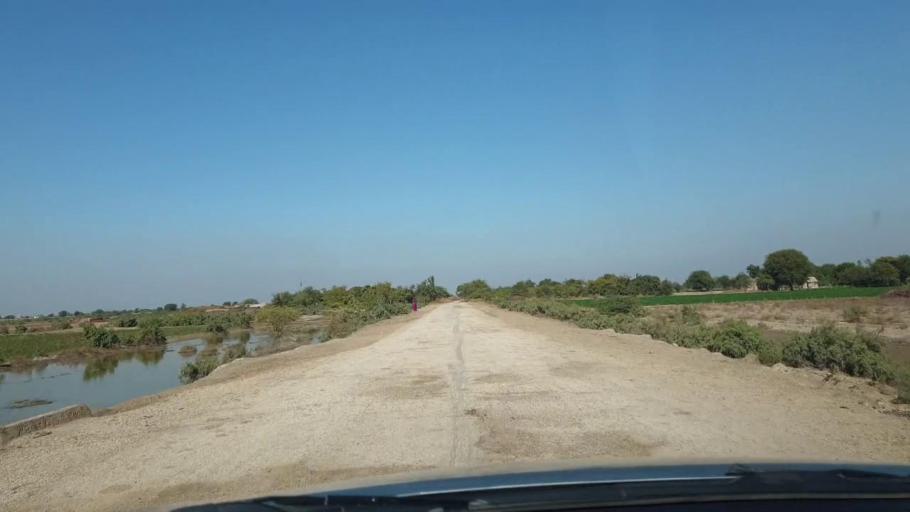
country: PK
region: Sindh
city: Jhol
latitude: 25.9264
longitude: 68.9080
